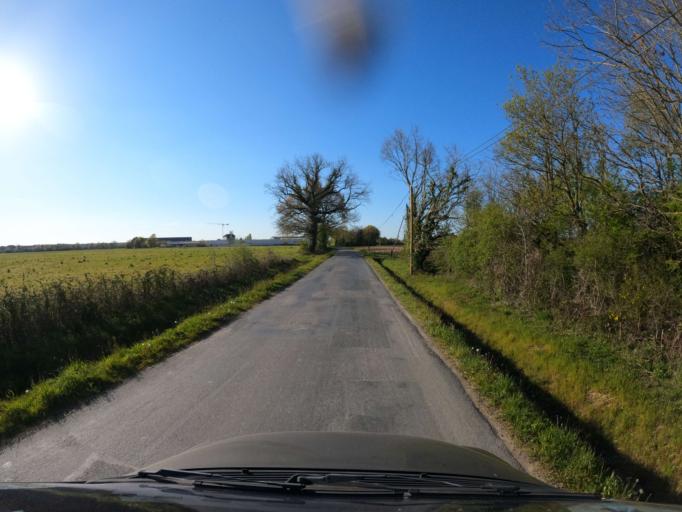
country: FR
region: Pays de la Loire
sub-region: Departement de la Vendee
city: Les Brouzils
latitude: 46.8986
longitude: -1.3712
